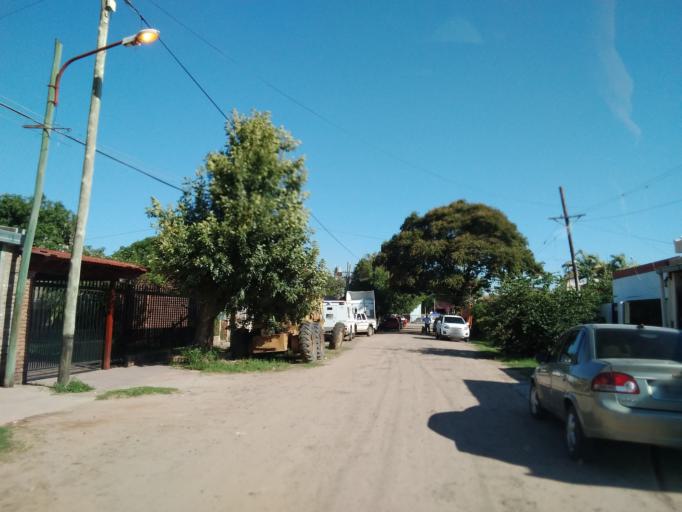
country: AR
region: Corrientes
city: Corrientes
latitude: -27.4860
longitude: -58.8037
